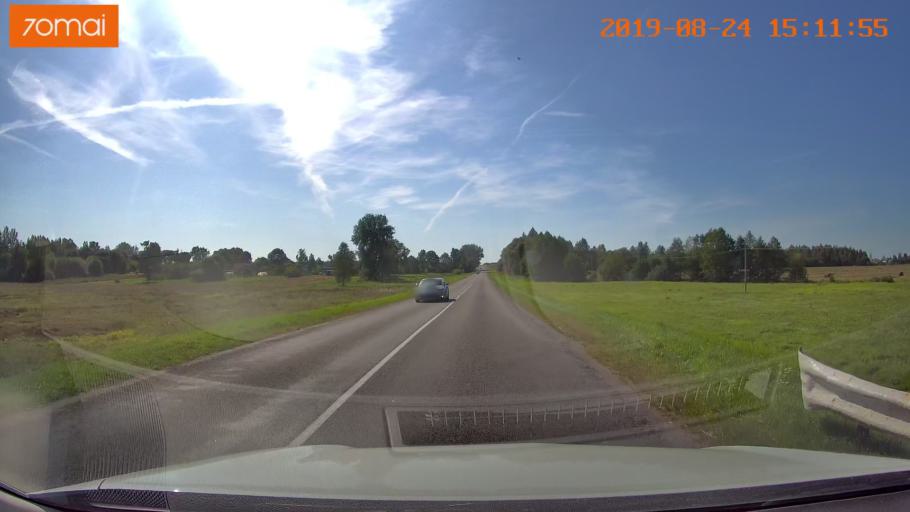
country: BY
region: Minsk
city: Samakhvalavichy
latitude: 53.6076
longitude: 27.5932
